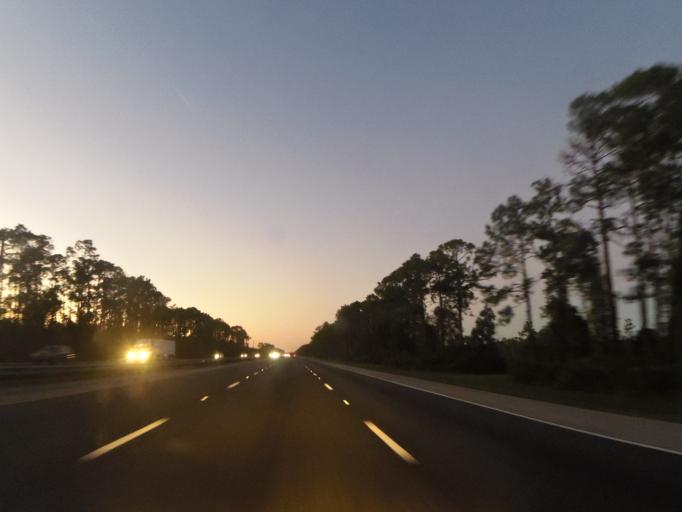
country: US
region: Florida
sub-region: Saint Johns County
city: Saint Augustine Shores
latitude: 29.7747
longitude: -81.3567
